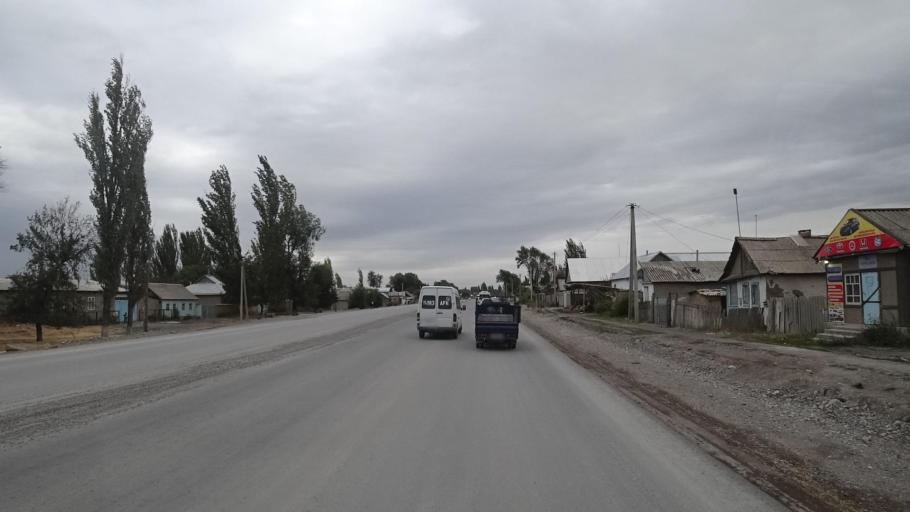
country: KG
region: Chuy
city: Belovodskoye
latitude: 42.8496
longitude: 74.1729
